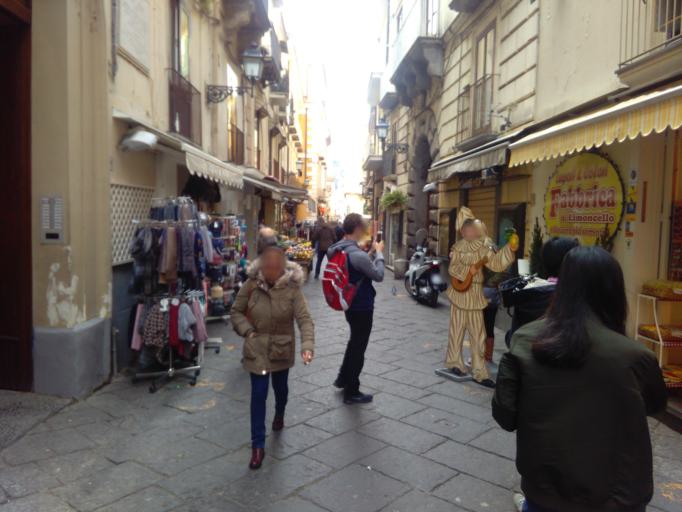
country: IT
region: Campania
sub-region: Provincia di Napoli
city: Sorrento
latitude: 40.6262
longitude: 14.3741
